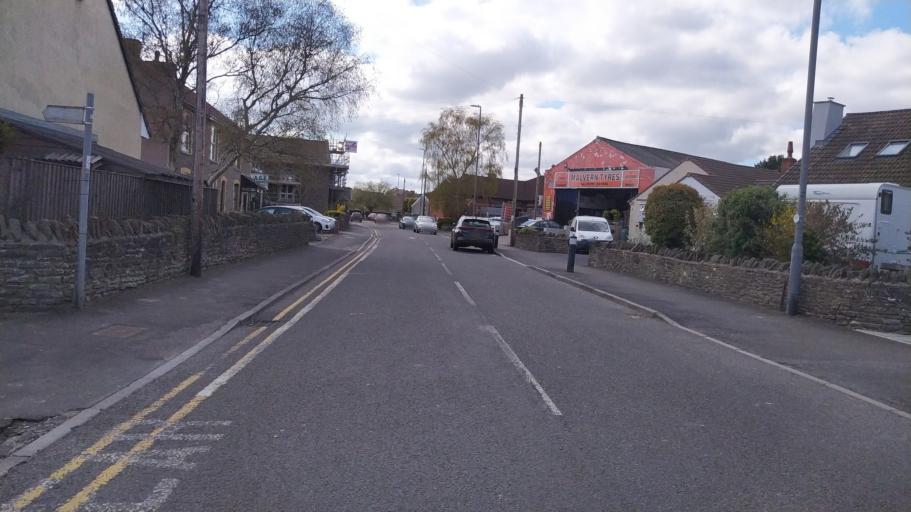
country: GB
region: England
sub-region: South Gloucestershire
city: Kingswood
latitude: 51.4388
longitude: -2.4929
